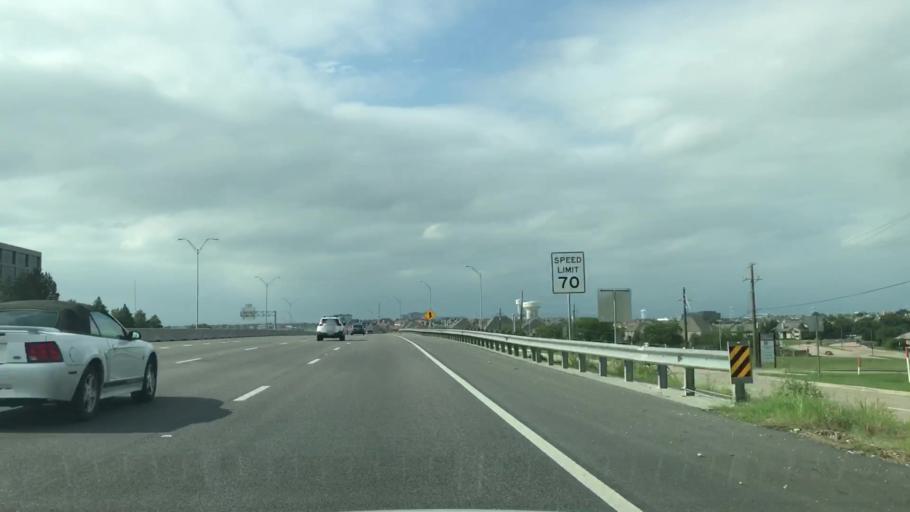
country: US
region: Texas
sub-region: Dallas County
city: Coppell
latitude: 32.8998
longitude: -96.9791
